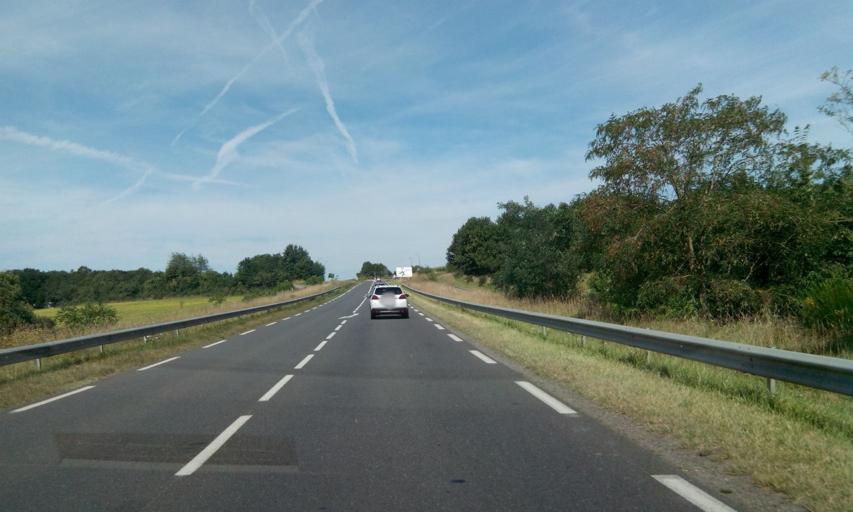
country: FR
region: Poitou-Charentes
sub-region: Departement de la Vienne
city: Charroux
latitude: 46.1486
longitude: 0.4108
